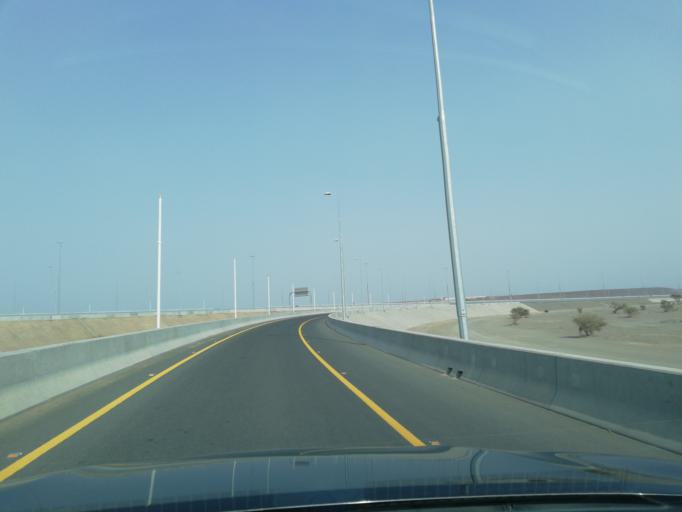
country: OM
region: Al Batinah
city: Al Liwa'
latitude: 24.3820
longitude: 56.5511
